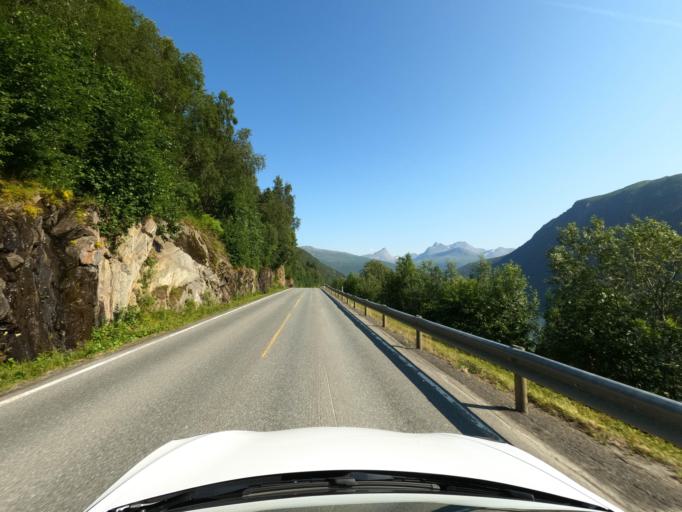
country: NO
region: Nordland
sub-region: Narvik
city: Narvik
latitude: 68.3960
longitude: 17.5171
